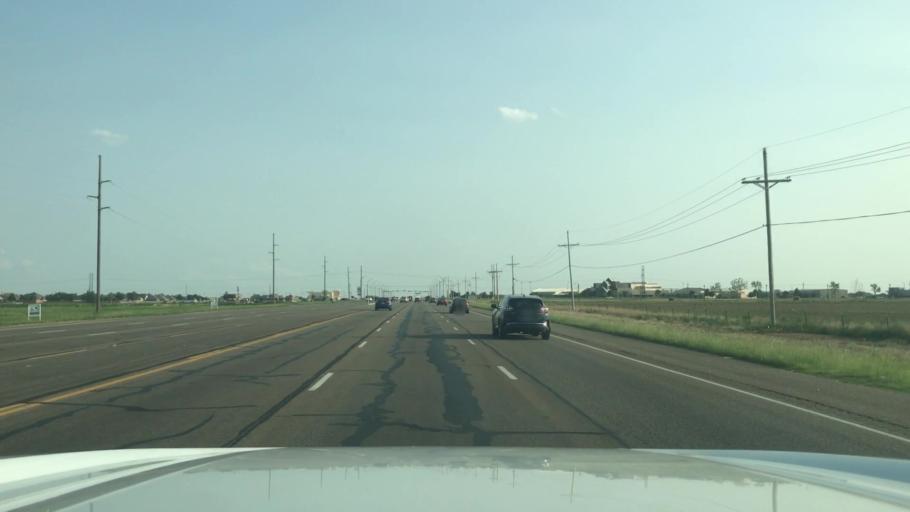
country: US
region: Texas
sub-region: Potter County
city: Amarillo
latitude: 35.1526
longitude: -101.9383
